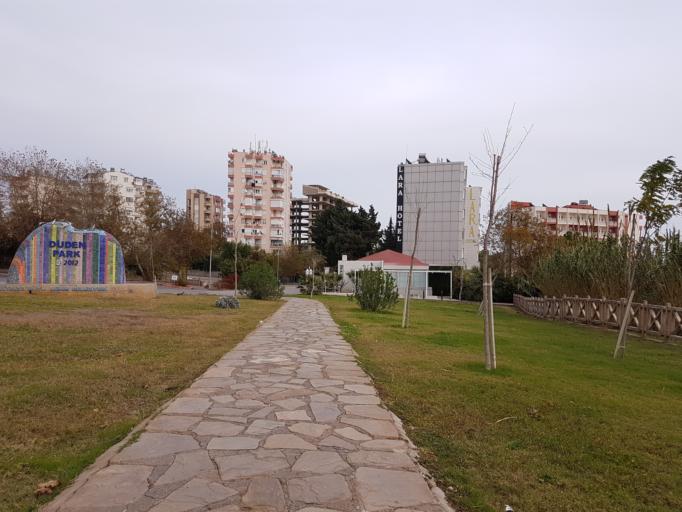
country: TR
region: Antalya
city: Antalya
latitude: 36.8531
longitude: 30.7883
